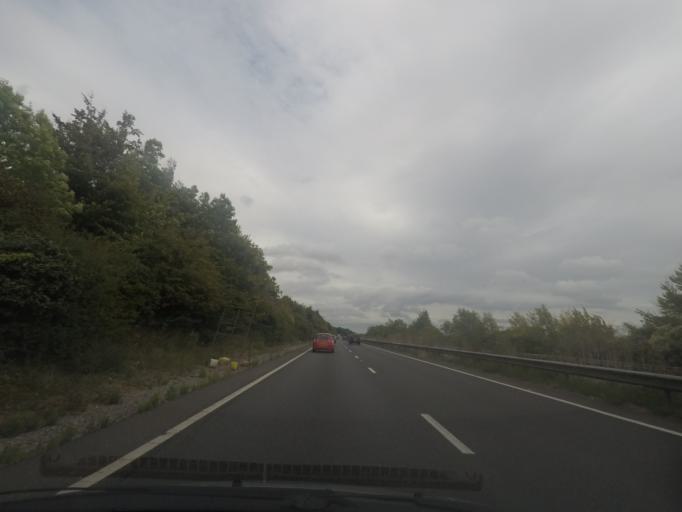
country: GB
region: England
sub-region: Hampshire
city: Abbotts Ann
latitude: 51.2145
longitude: -1.5422
